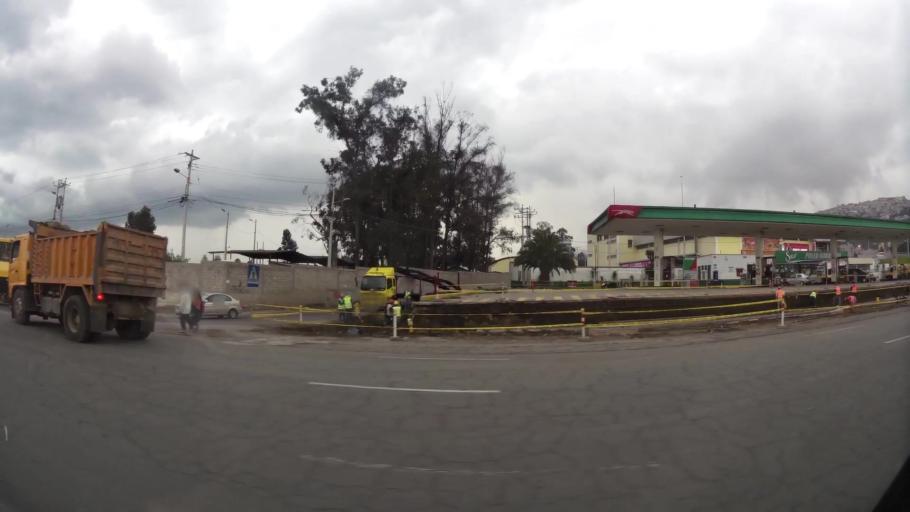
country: EC
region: Pichincha
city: Quito
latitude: -0.1091
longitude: -78.4568
